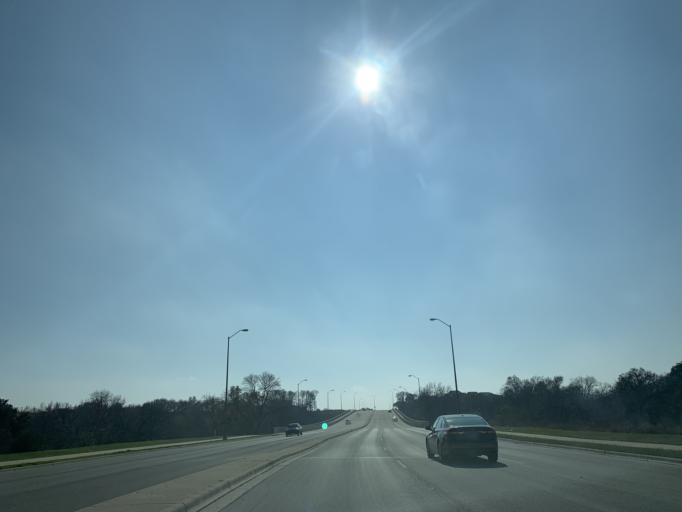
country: US
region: Texas
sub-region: Williamson County
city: Round Rock
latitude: 30.5155
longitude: -97.6367
